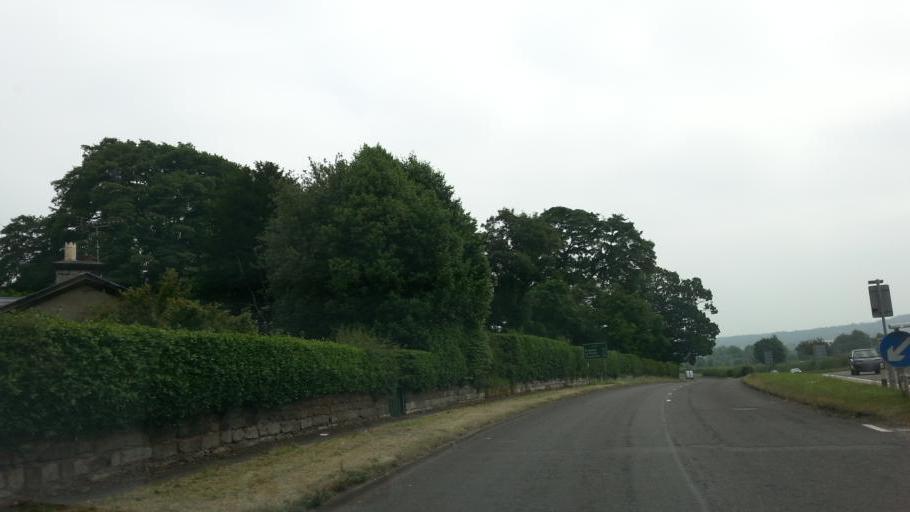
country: GB
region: England
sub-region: Staffordshire
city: Stafford
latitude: 52.8606
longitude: -2.0771
